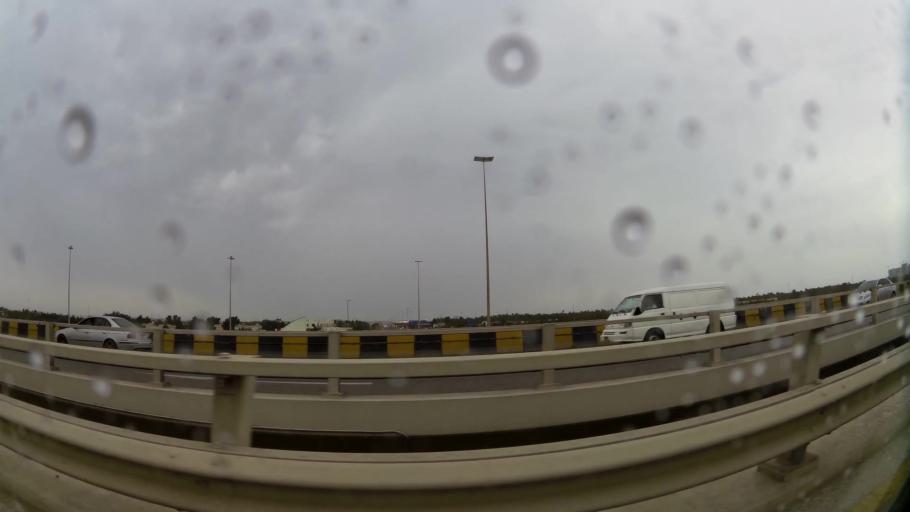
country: BH
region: Central Governorate
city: Madinat Hamad
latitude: 26.1728
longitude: 50.4655
